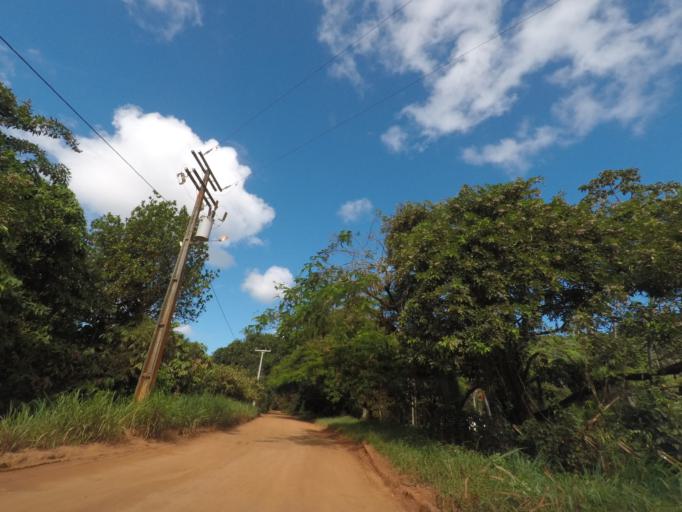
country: BR
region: Bahia
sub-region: Itacare
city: Itacare
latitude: -14.2110
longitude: -39.0515
